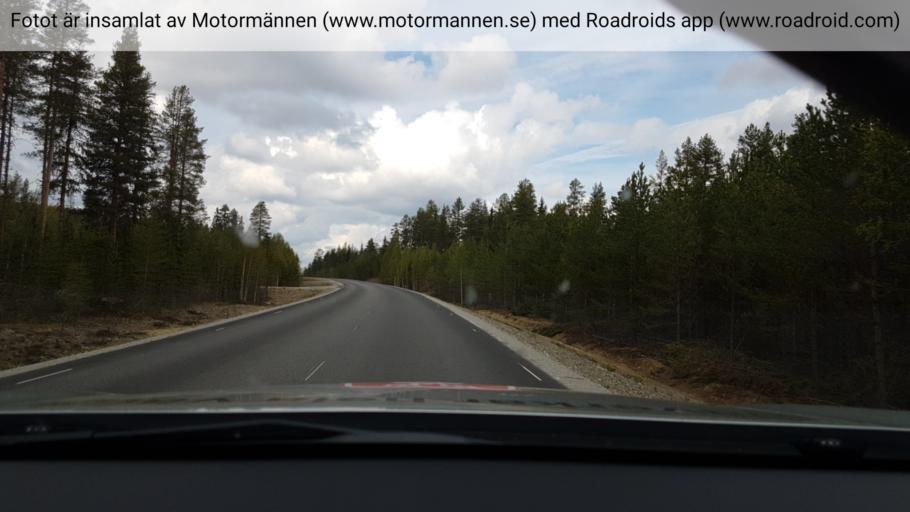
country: SE
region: Vaesterbotten
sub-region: Lycksele Kommun
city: Lycksele
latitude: 64.0224
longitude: 18.4500
